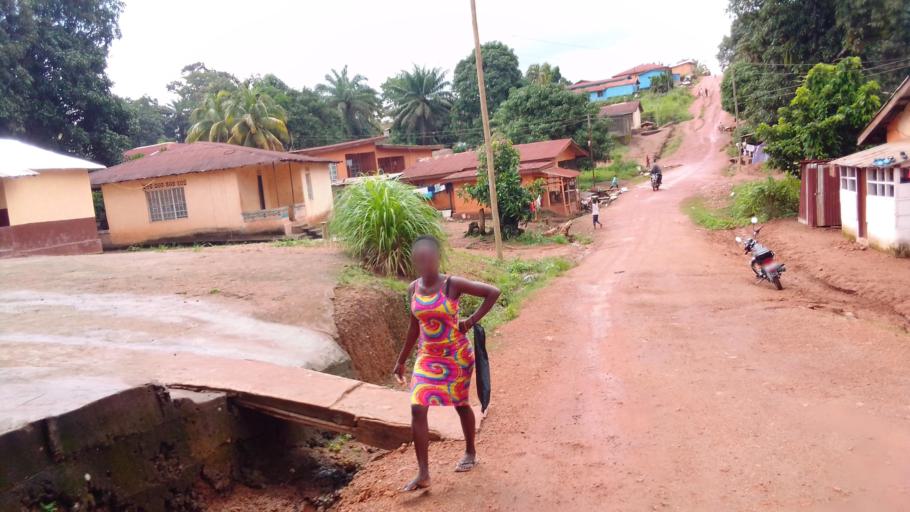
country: SL
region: Eastern Province
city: Kenema
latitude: 7.8737
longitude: -11.1783
